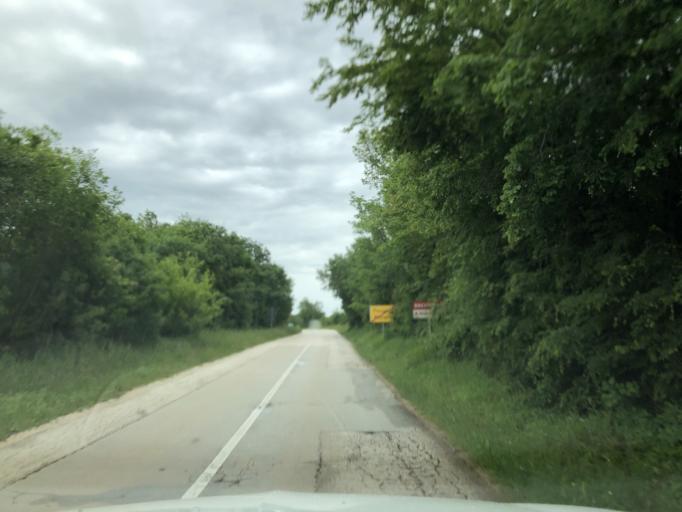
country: HR
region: Istarska
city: Buje
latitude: 45.4482
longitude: 13.6395
